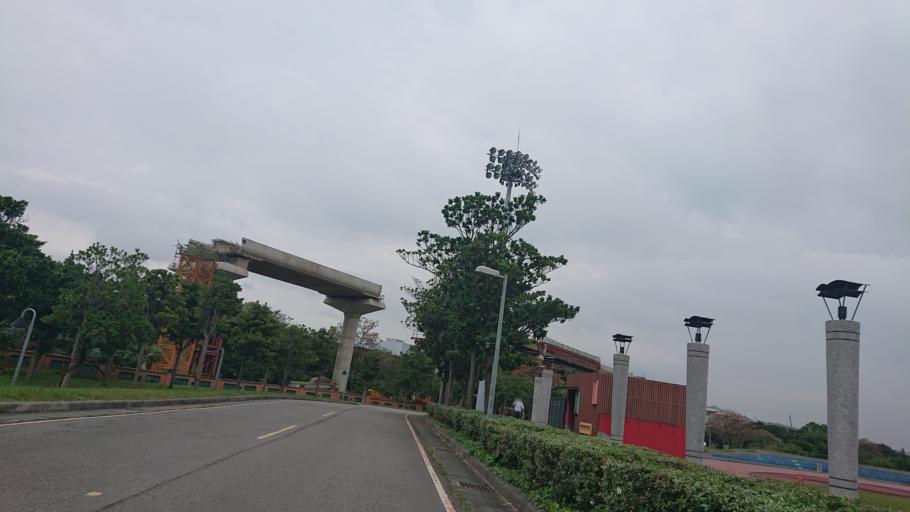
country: TW
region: Taiwan
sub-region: Taoyuan
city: Taoyuan
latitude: 24.9401
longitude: 121.3628
